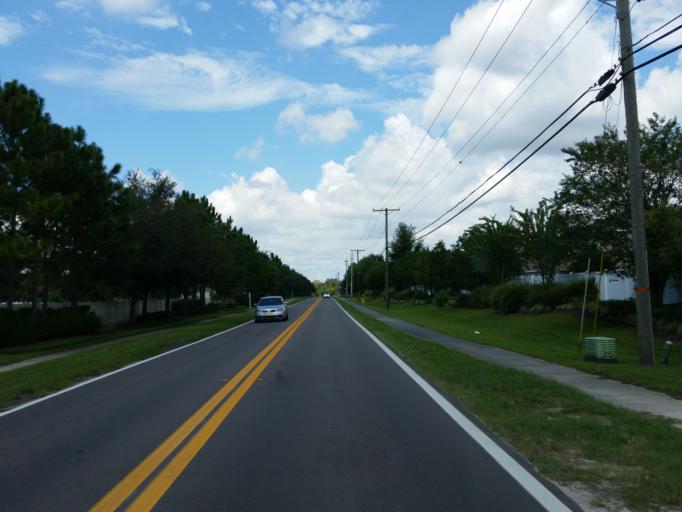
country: US
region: Florida
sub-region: Hillsborough County
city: Riverview
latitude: 27.8350
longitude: -82.3076
